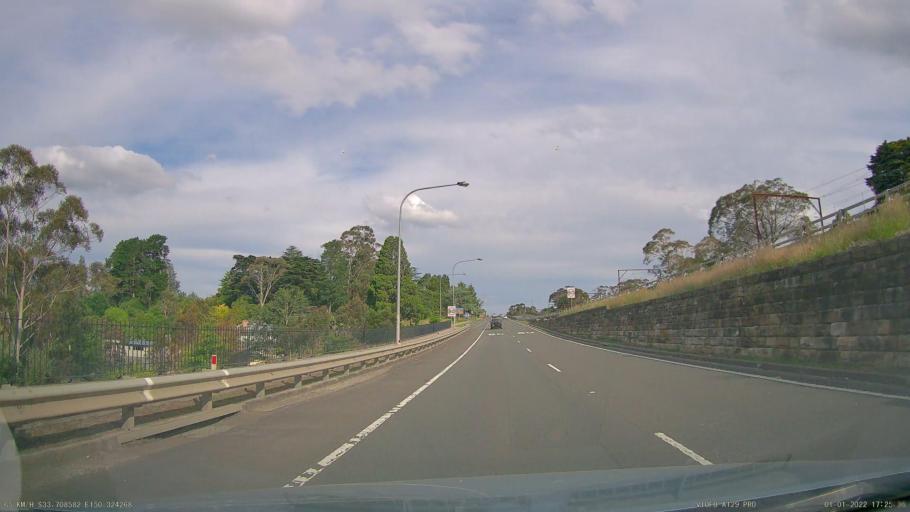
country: AU
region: New South Wales
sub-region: Blue Mountains Municipality
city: Leura
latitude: -33.7087
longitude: 150.3245
